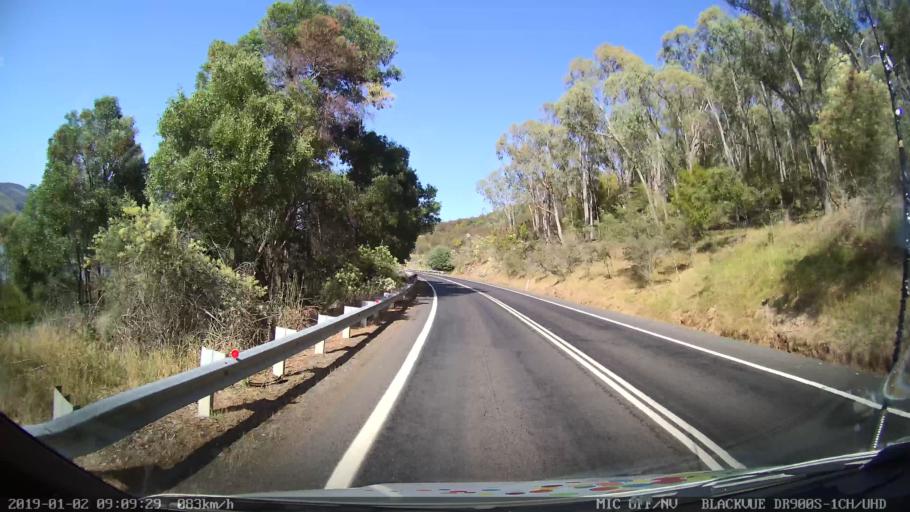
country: AU
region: New South Wales
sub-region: Tumut Shire
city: Tumut
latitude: -35.5248
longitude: 148.2789
